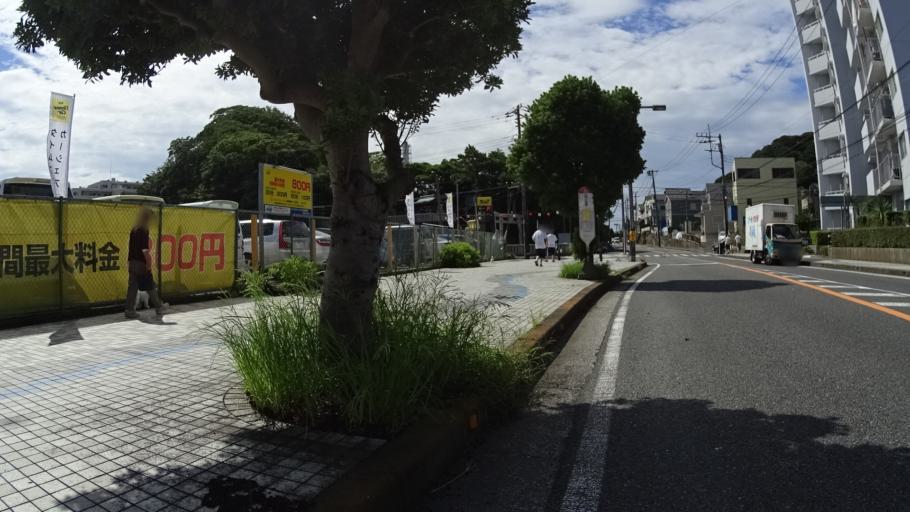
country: JP
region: Kanagawa
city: Yokosuka
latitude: 35.2196
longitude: 139.7133
